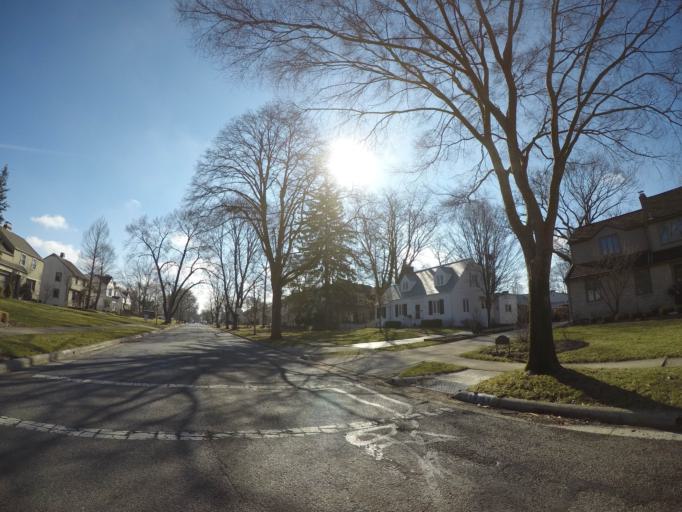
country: US
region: Ohio
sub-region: Franklin County
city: Upper Arlington
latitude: 40.0007
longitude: -83.0517
